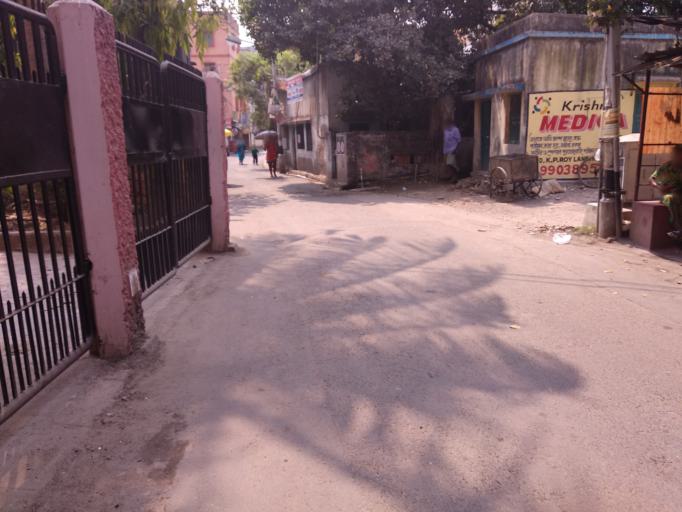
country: IN
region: West Bengal
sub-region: Kolkata
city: Kolkata
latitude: 22.5048
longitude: 88.3762
